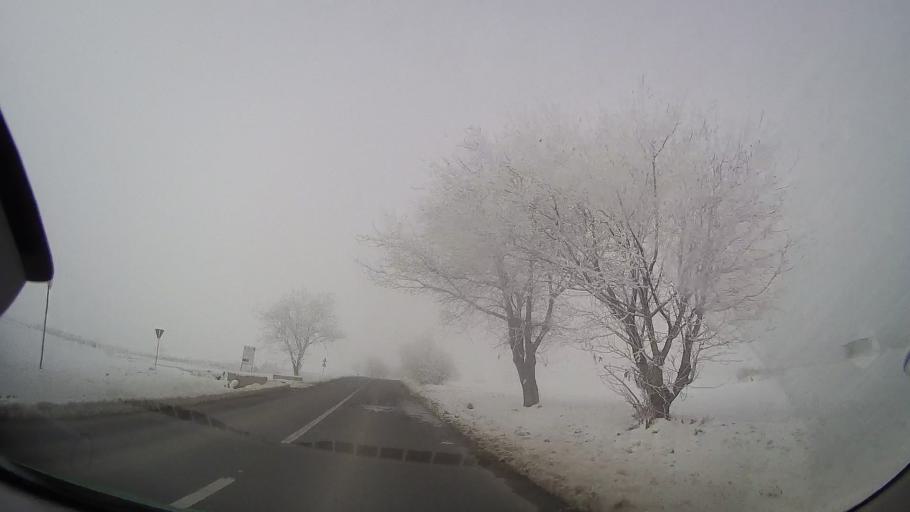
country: RO
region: Iasi
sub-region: Comuna Stolniceni-Prajescu
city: Stolniceni-Prajescu
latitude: 47.1869
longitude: 26.7383
